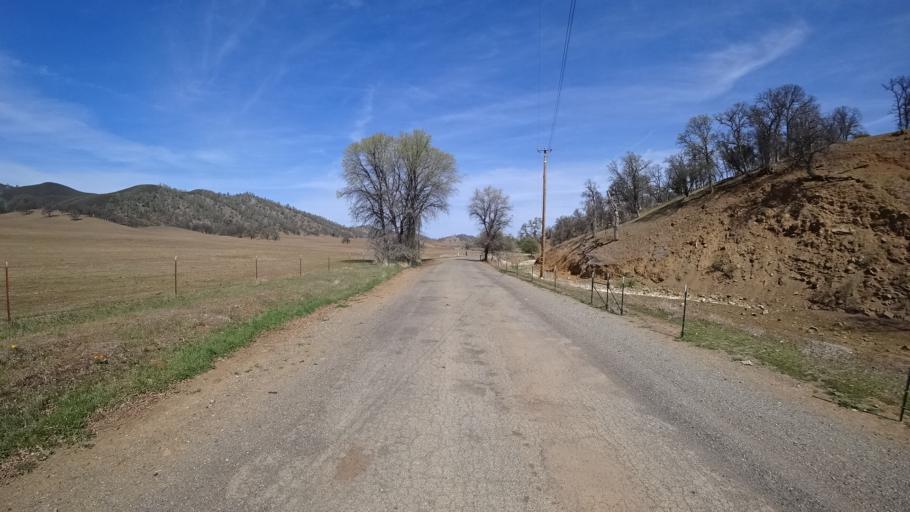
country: US
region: California
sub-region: Glenn County
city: Willows
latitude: 39.4721
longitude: -122.4488
